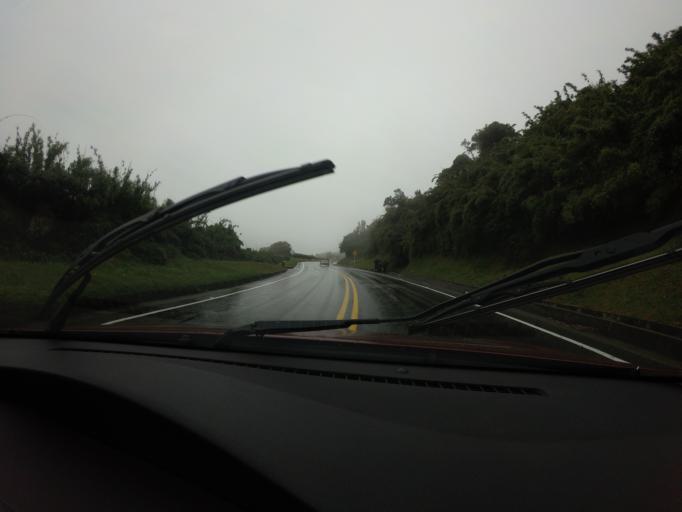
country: CO
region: Caldas
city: Villamaria
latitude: 5.0161
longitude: -75.3393
